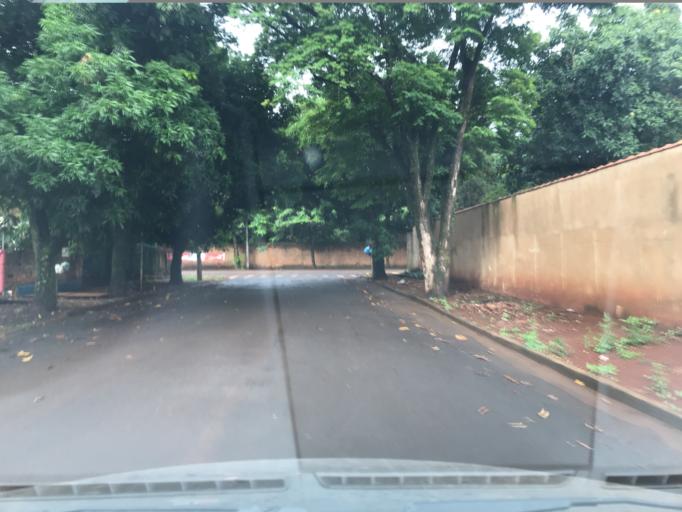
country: BR
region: Parana
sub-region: Palotina
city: Palotina
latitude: -24.2923
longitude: -53.8452
